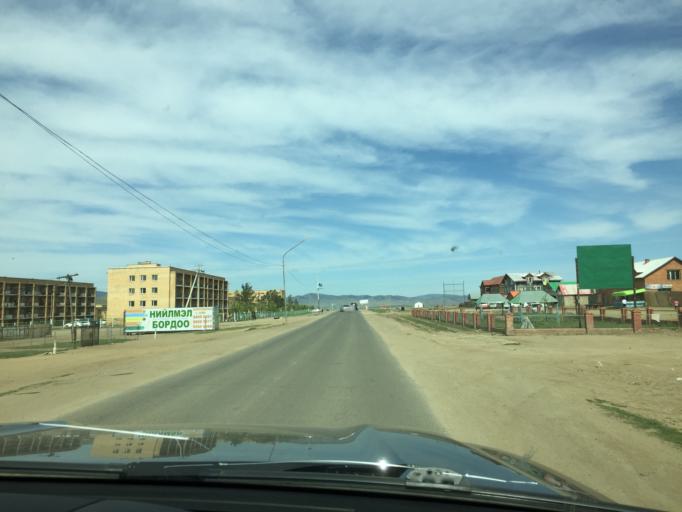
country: MN
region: Central Aimak
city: Ihsueuej
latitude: 48.2250
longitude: 106.2924
